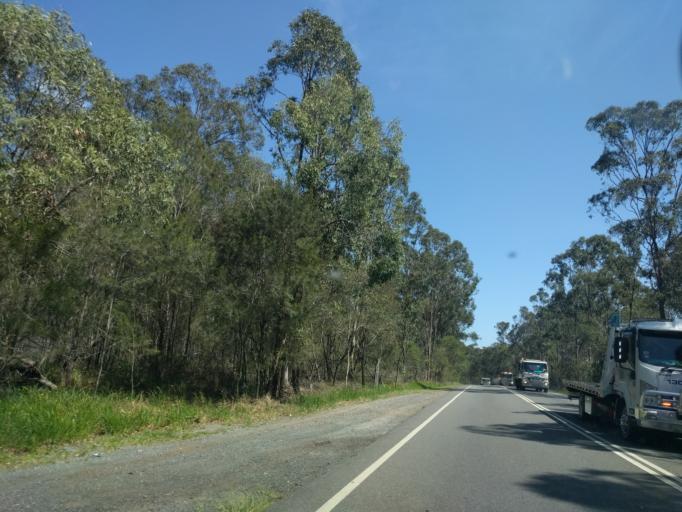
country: AU
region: Queensland
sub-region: Brisbane
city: Forest Lake
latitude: -27.6419
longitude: 152.9748
